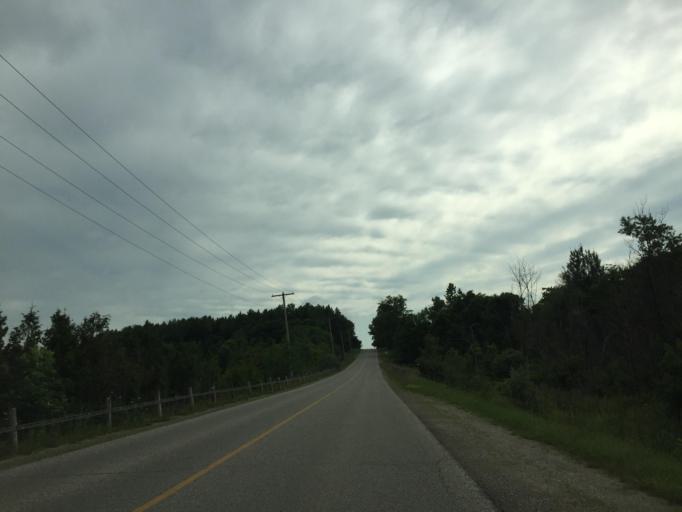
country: CA
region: Ontario
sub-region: Wellington County
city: Guelph
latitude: 43.6008
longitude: -80.2638
